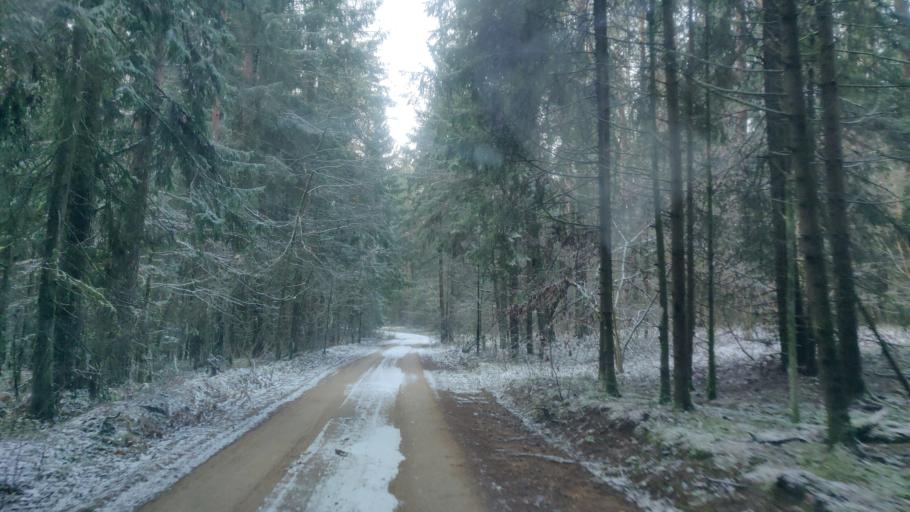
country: LT
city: Trakai
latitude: 54.5776
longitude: 24.9450
